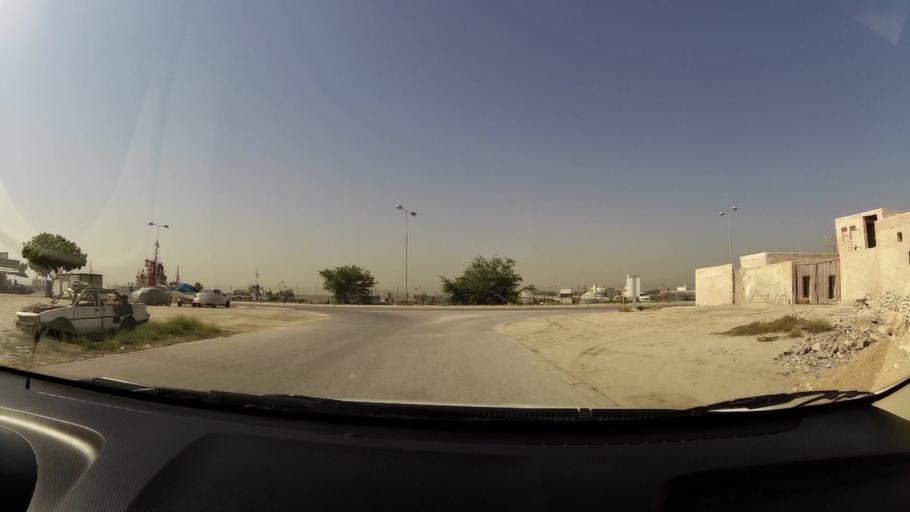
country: AE
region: Umm al Qaywayn
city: Umm al Qaywayn
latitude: 25.5823
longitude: 55.5699
